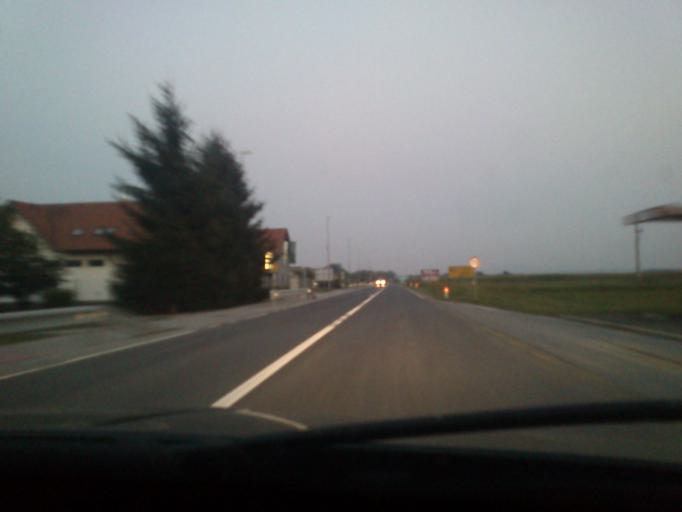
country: SI
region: Kidricevo
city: Kidricevo
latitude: 46.4367
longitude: 15.8142
